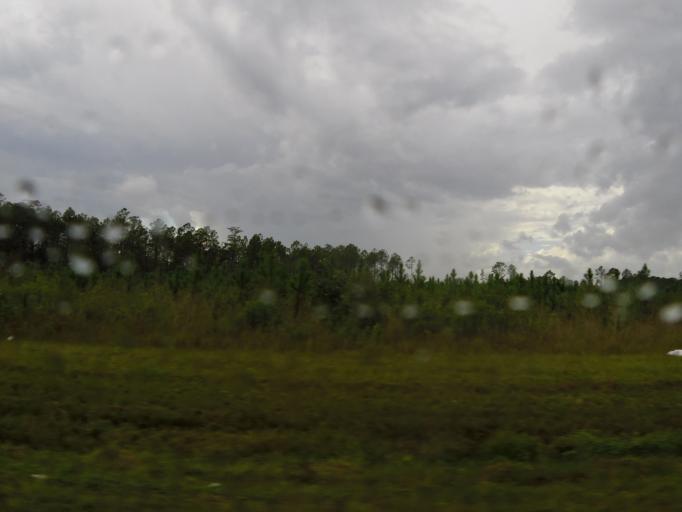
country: US
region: Florida
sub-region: Nassau County
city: Callahan
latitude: 30.4870
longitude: -81.9994
